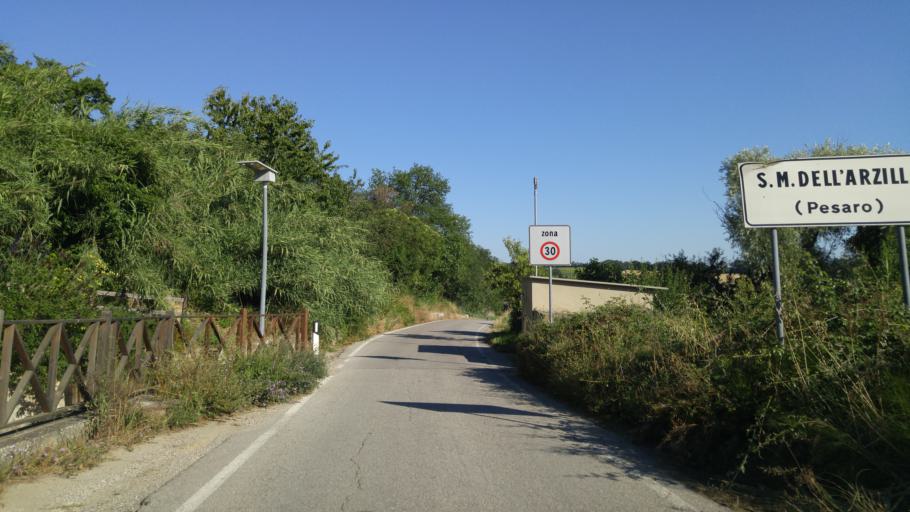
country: IT
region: The Marches
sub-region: Provincia di Pesaro e Urbino
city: Pesaro
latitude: 43.8448
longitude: 12.8943
